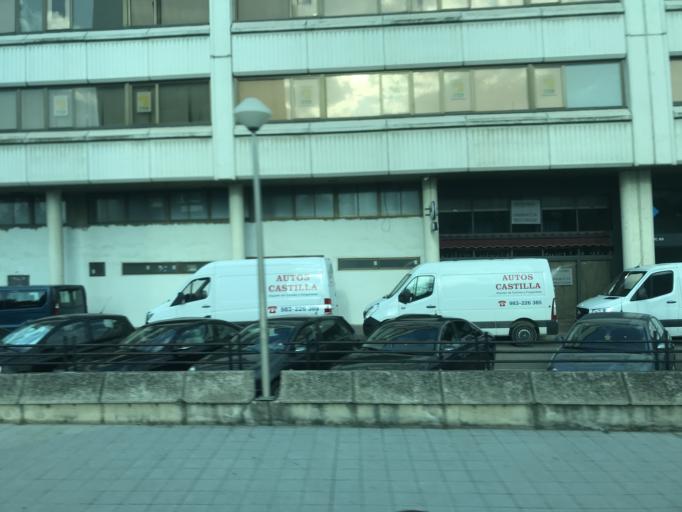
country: ES
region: Castille and Leon
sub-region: Provincia de Valladolid
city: Valladolid
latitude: 41.6270
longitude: -4.7268
